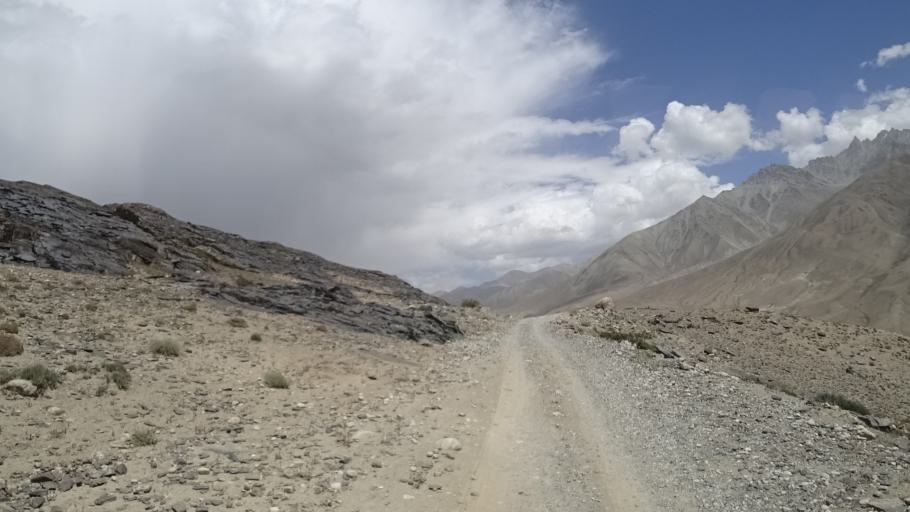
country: AF
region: Badakhshan
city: Khandud
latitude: 37.0960
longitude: 72.7094
